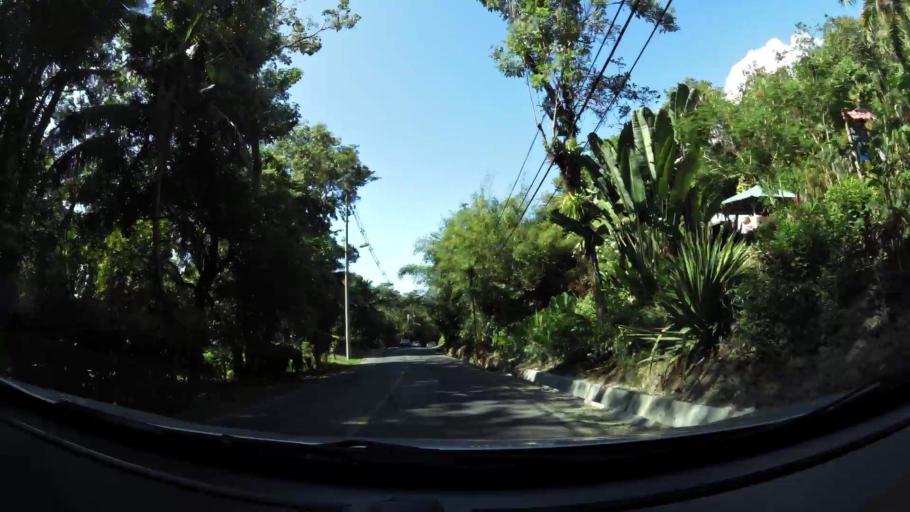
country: CR
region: Puntarenas
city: Quepos
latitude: 9.4241
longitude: -84.1588
